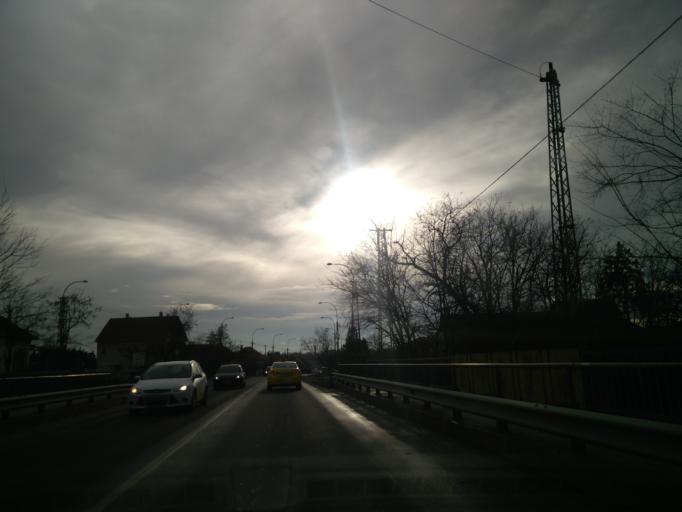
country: HU
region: Pest
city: Fot
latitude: 47.6154
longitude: 19.1969
